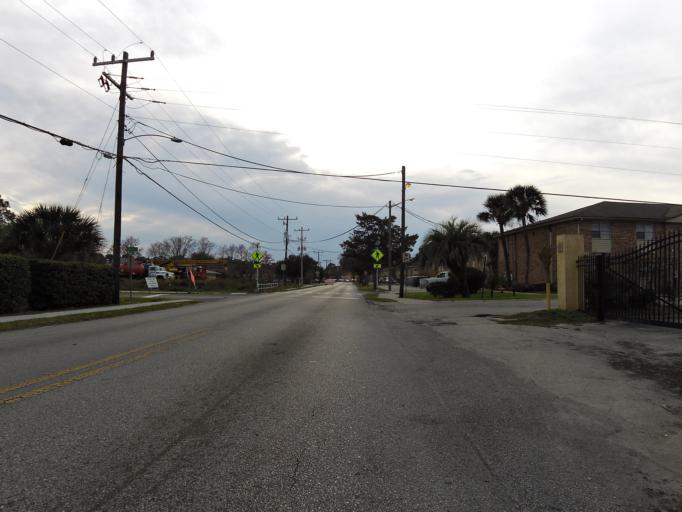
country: US
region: Florida
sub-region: Duval County
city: Jacksonville
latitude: 30.2516
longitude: -81.6185
